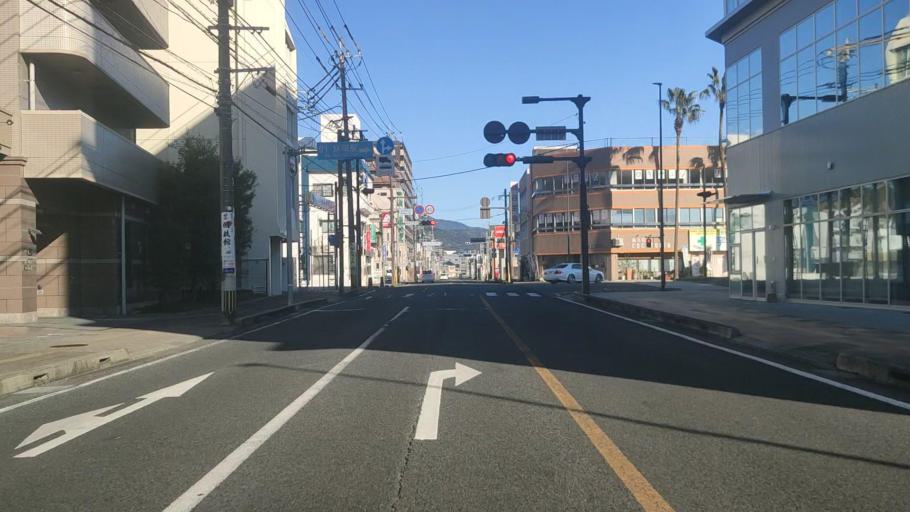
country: JP
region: Miyazaki
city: Nobeoka
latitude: 32.5893
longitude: 131.6712
